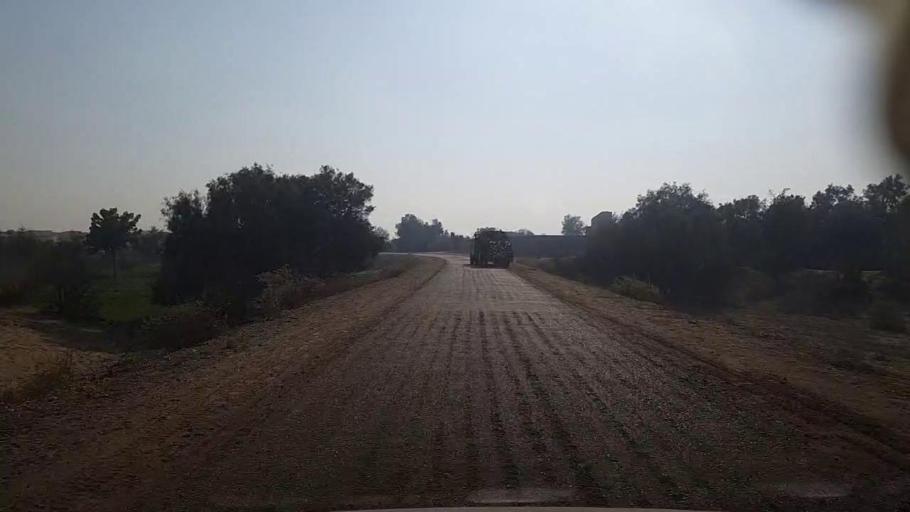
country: PK
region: Sindh
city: Kandiari
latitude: 26.8296
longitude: 68.4892
